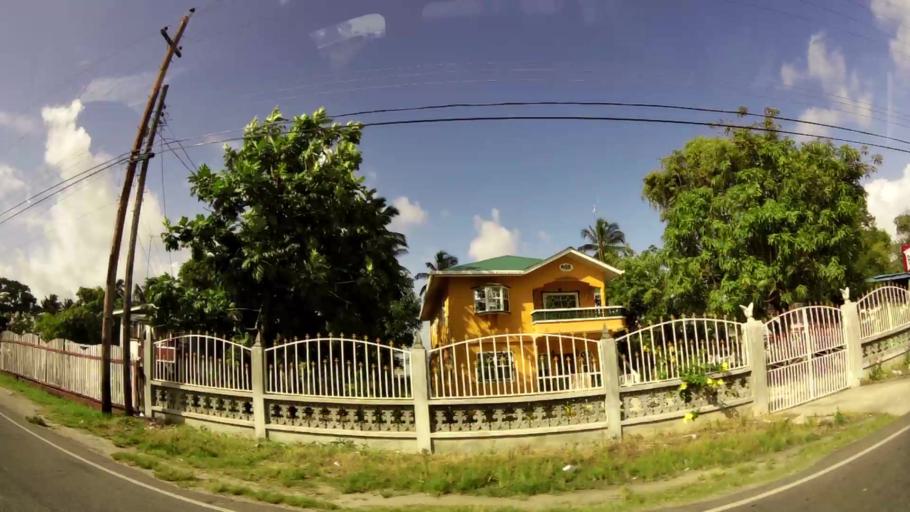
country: GY
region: Demerara-Mahaica
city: Mahaica Village
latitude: 6.7514
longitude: -57.9711
